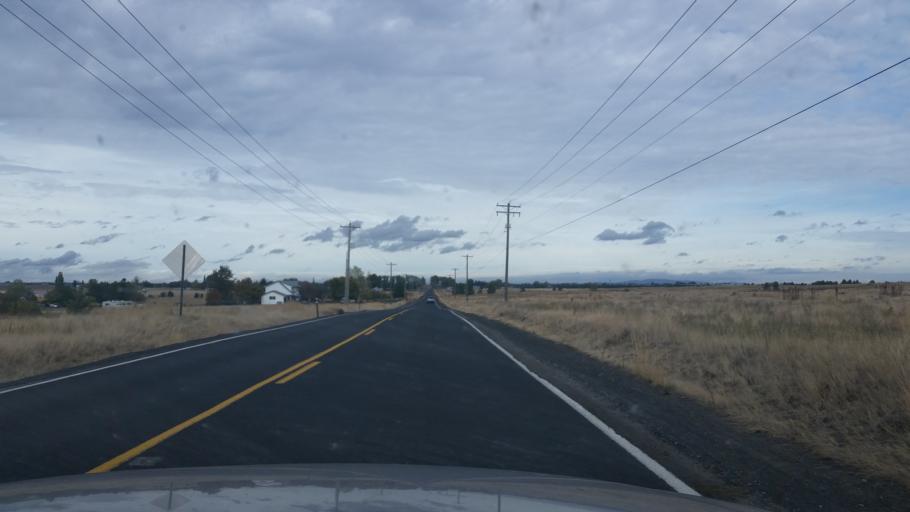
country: US
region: Washington
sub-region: Spokane County
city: Fairchild Air Force Base
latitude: 47.5957
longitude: -117.6075
